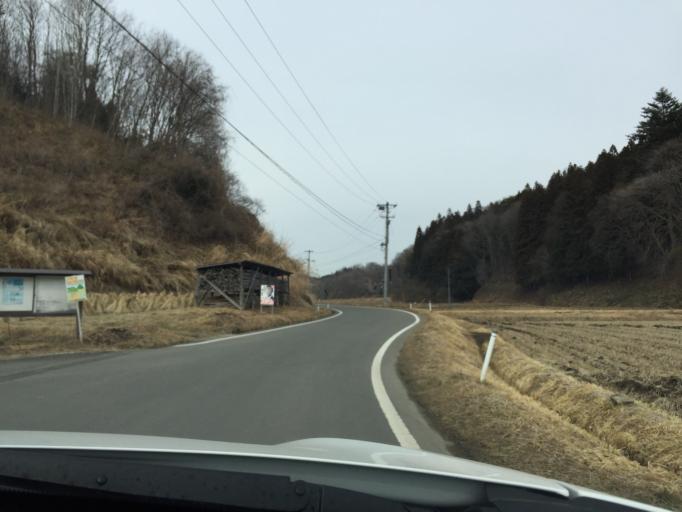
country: JP
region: Fukushima
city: Ishikawa
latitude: 37.1898
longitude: 140.5726
